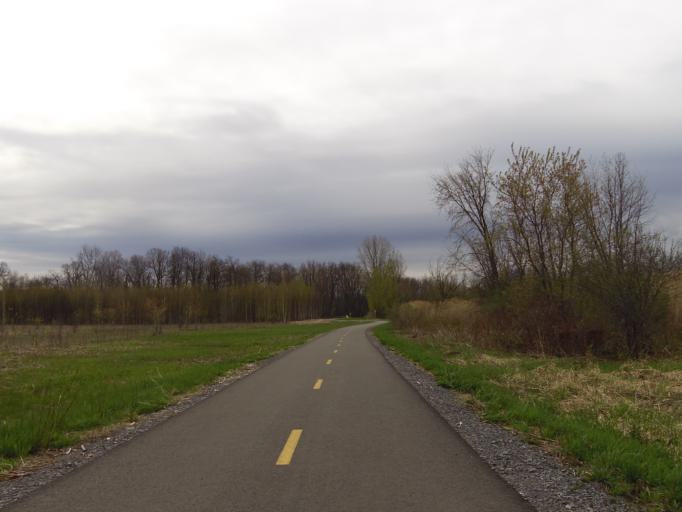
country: CA
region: Quebec
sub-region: Laurentides
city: Oka
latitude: 45.4717
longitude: -74.0662
